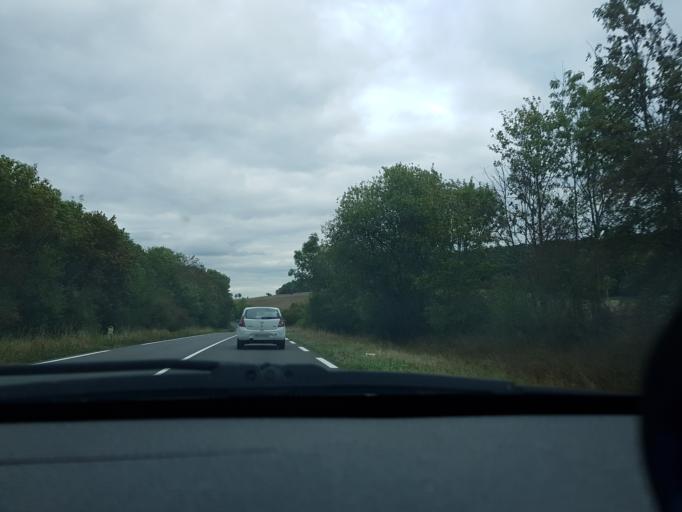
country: FR
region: Lorraine
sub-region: Departement de la Moselle
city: Chateau-Salins
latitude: 48.7778
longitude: 6.4630
